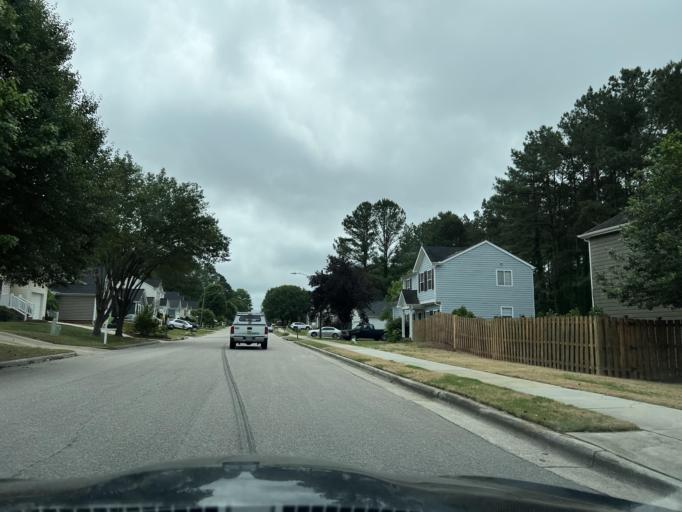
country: US
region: North Carolina
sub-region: Wake County
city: Knightdale
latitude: 35.8665
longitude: -78.5505
